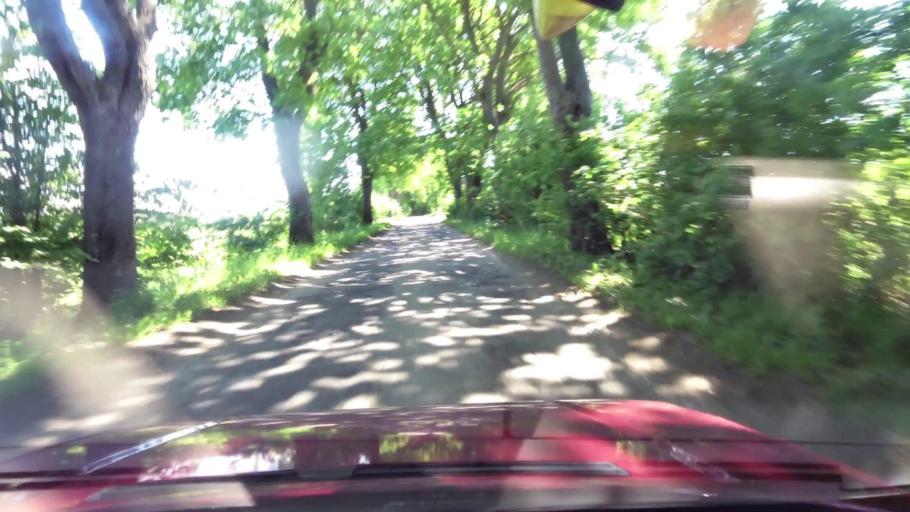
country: PL
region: West Pomeranian Voivodeship
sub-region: Powiat koszalinski
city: Bobolice
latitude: 54.0138
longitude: 16.6557
